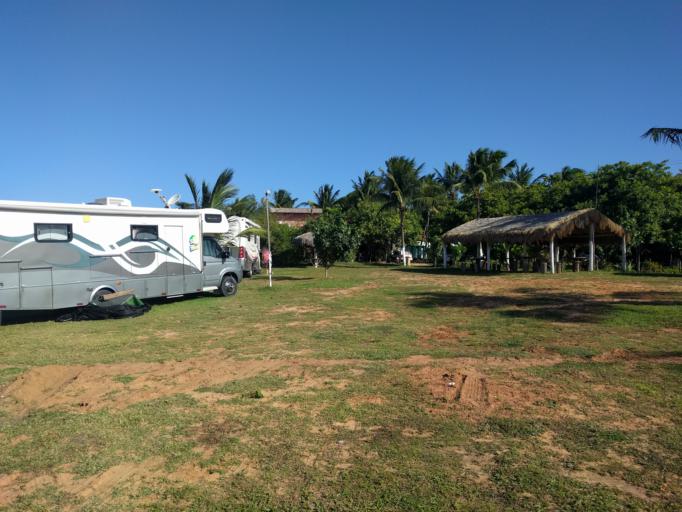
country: BR
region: Rio Grande do Norte
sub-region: Ares
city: Ares
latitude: -6.2321
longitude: -35.0423
